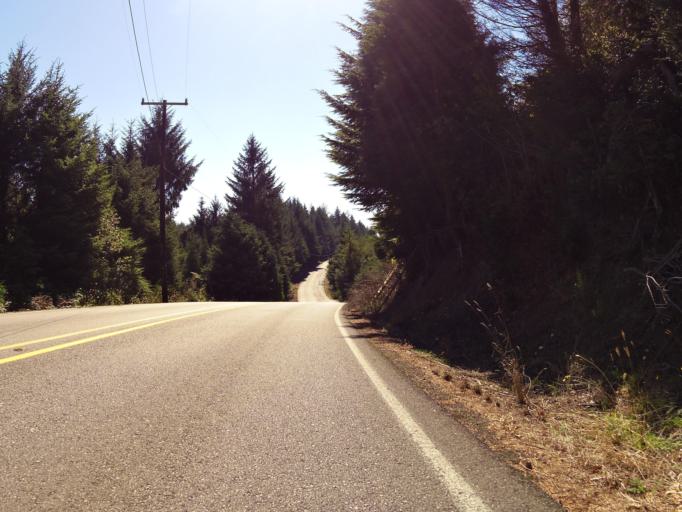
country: US
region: Oregon
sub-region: Coos County
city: Barview
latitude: 43.3259
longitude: -124.3414
